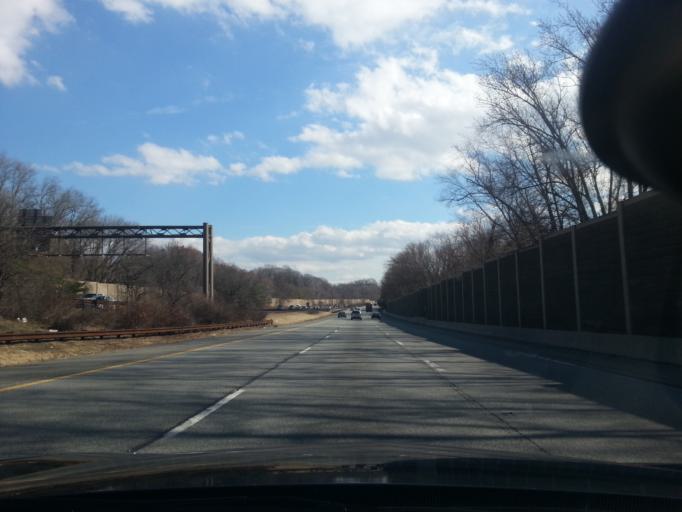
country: US
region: Pennsylvania
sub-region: Delaware County
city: Radnor
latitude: 40.0209
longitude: -75.3605
